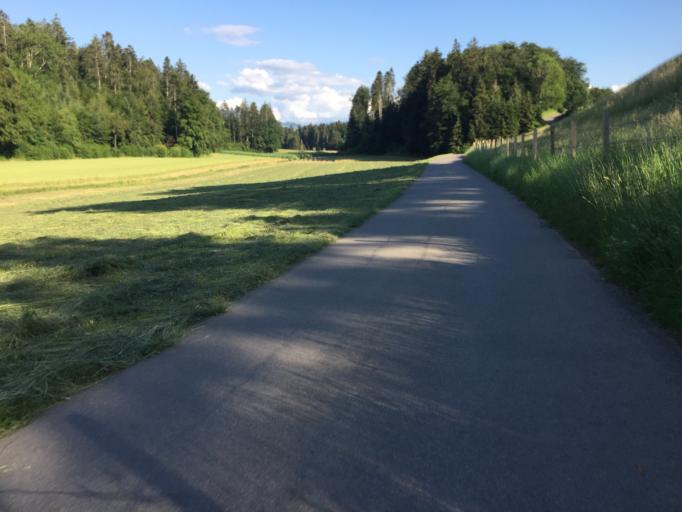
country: CH
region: Bern
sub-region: Bern-Mittelland District
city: Niederwichtrach
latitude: 46.8389
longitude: 7.5821
